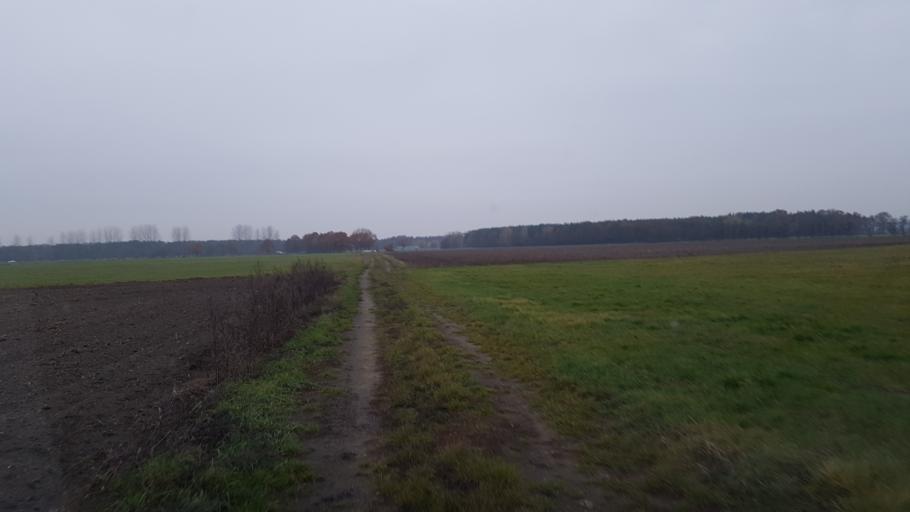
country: DE
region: Brandenburg
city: Schilda
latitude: 51.6210
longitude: 13.3378
